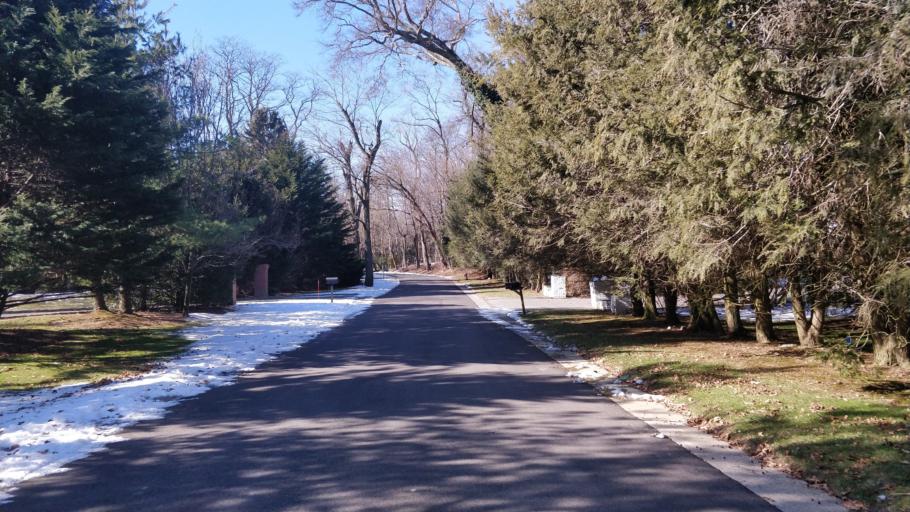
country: US
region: New York
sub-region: Nassau County
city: New Cassel
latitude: 40.7756
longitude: -73.5818
